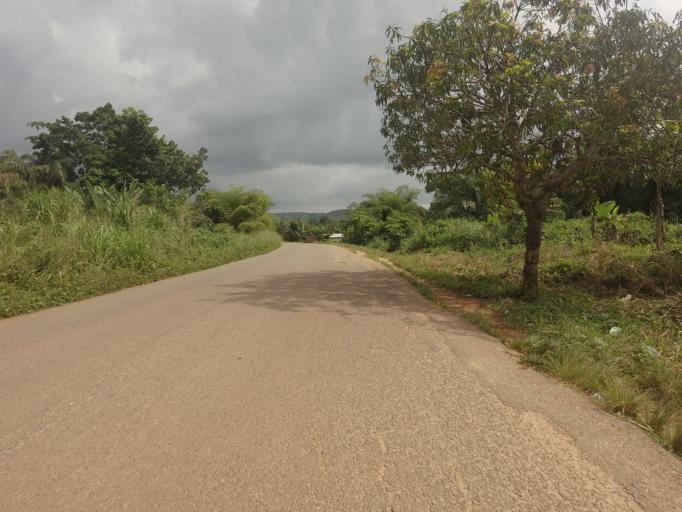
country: GH
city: Akropong
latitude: 5.9549
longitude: -0.1642
